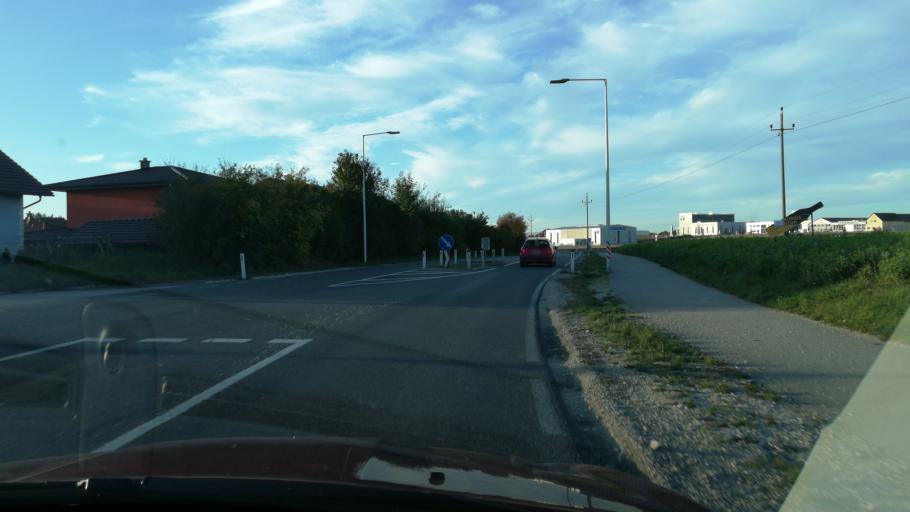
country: AT
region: Upper Austria
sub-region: Politischer Bezirk Steyr-Land
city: Bad Hall
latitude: 48.0226
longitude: 14.2317
